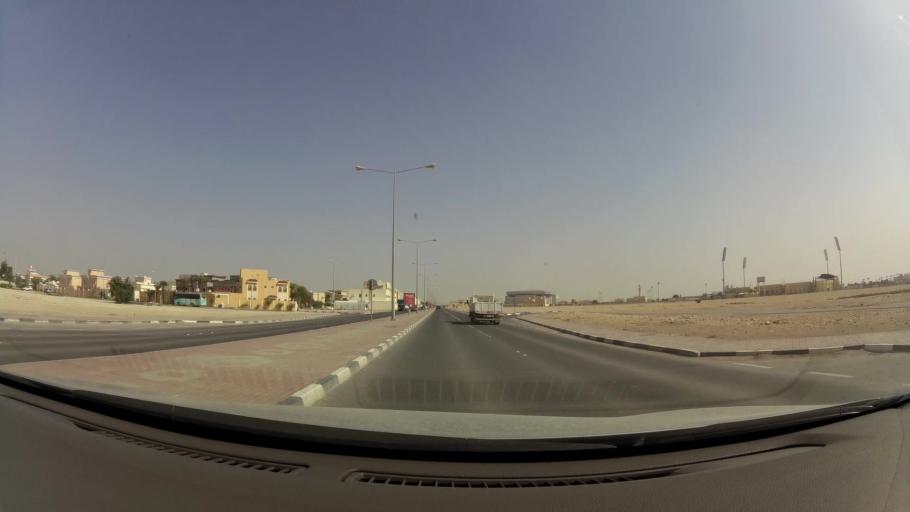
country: QA
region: Baladiyat ar Rayyan
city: Ar Rayyan
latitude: 25.3507
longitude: 51.4407
